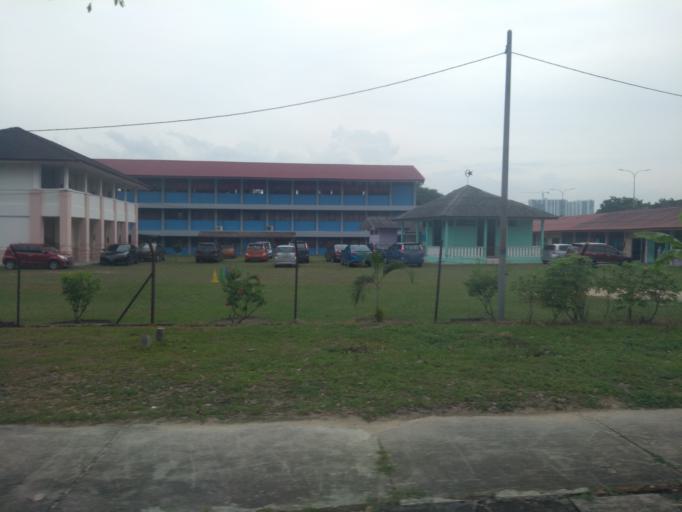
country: MY
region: Johor
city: Johor Bahru
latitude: 1.4941
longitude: 103.7046
